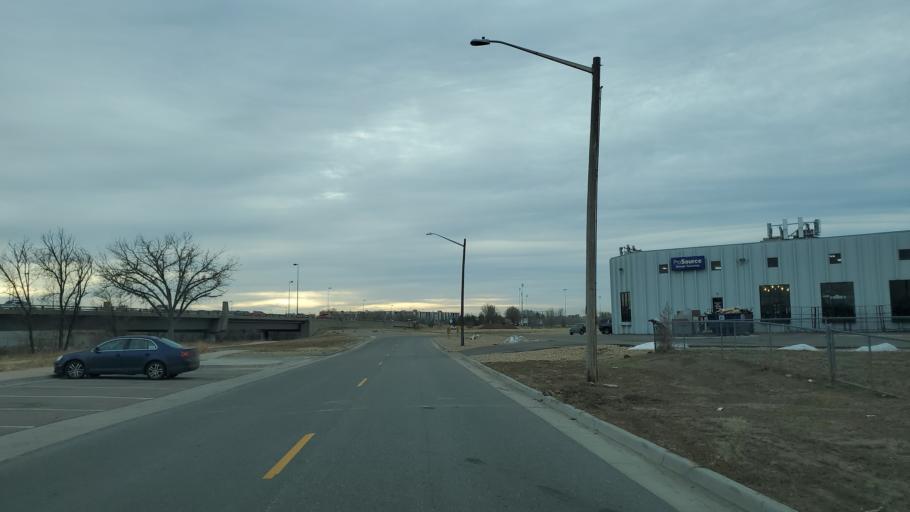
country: US
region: Colorado
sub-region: Denver County
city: Denver
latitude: 39.7042
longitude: -104.9975
